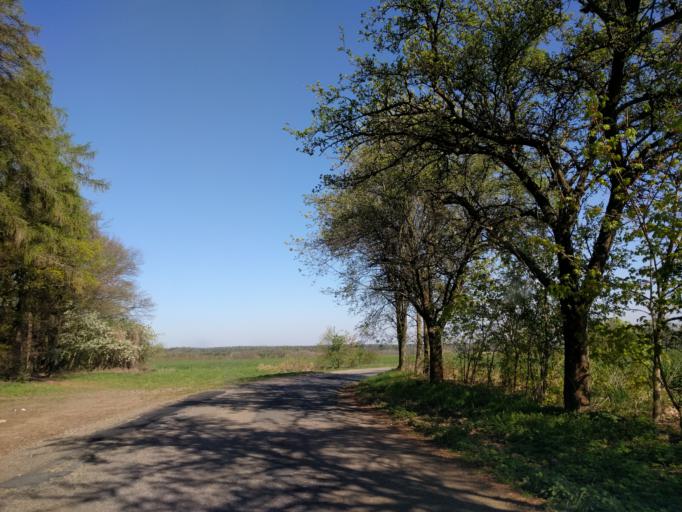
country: CZ
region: Central Bohemia
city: Mukarov
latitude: 49.9954
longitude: 14.7740
